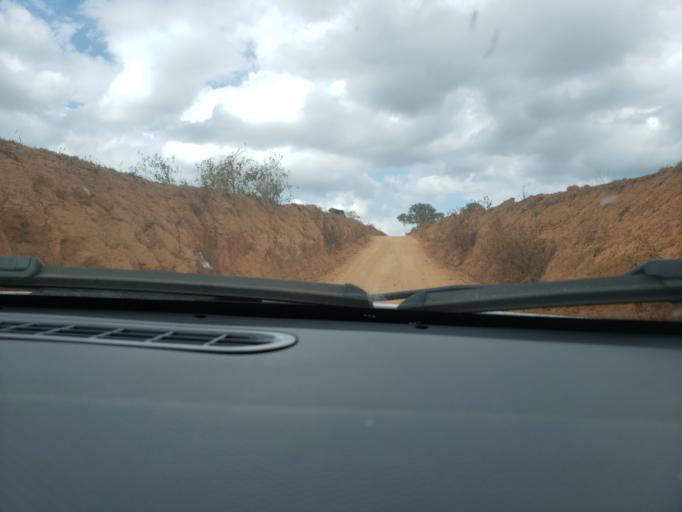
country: BR
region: Minas Gerais
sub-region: Campo Belo
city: Campo Belo
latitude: -20.9169
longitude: -45.2993
